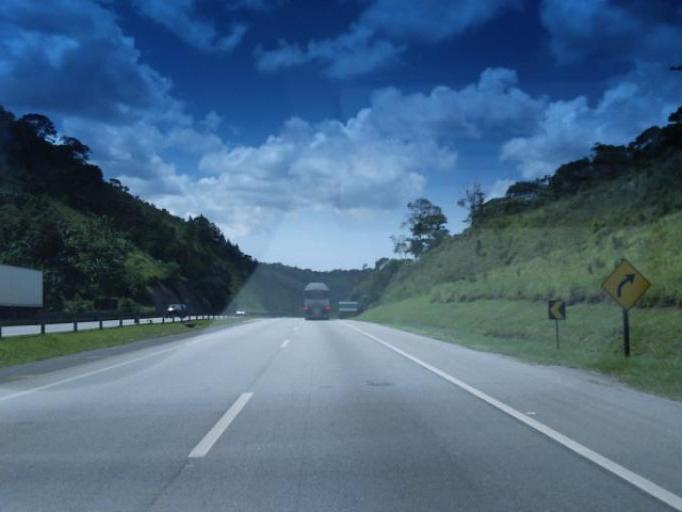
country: BR
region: Sao Paulo
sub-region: Juquitiba
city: Juquitiba
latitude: -23.9900
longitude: -47.1484
